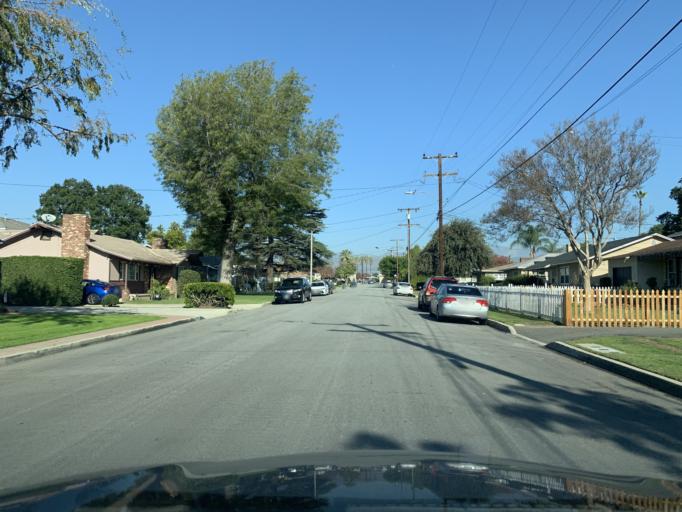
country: US
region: California
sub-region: Los Angeles County
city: Covina
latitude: 34.0841
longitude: -117.8802
